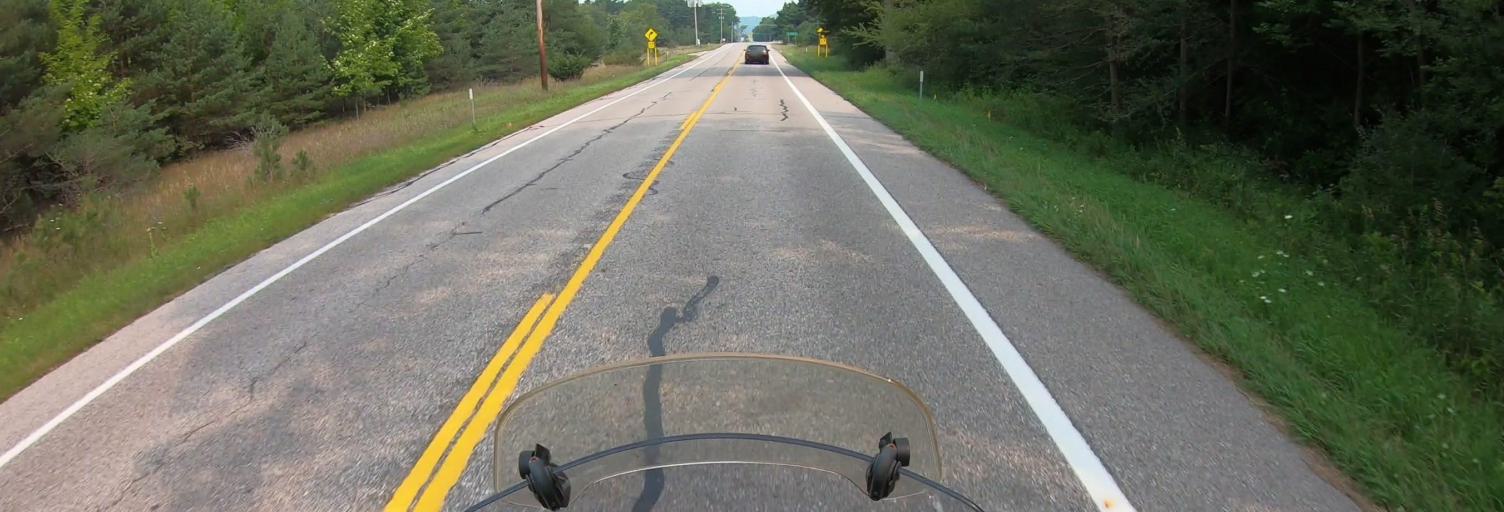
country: US
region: Michigan
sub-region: Benzie County
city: Beulah
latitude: 44.8519
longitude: -86.0137
